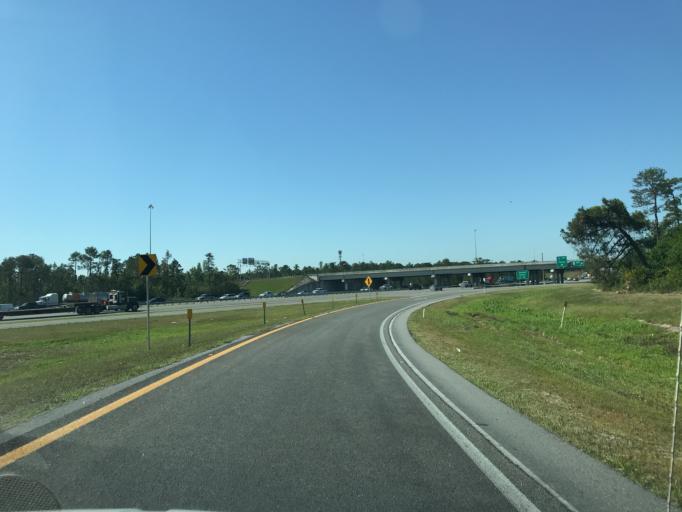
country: US
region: Florida
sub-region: Osceola County
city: Celebration
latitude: 28.3619
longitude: -81.5199
